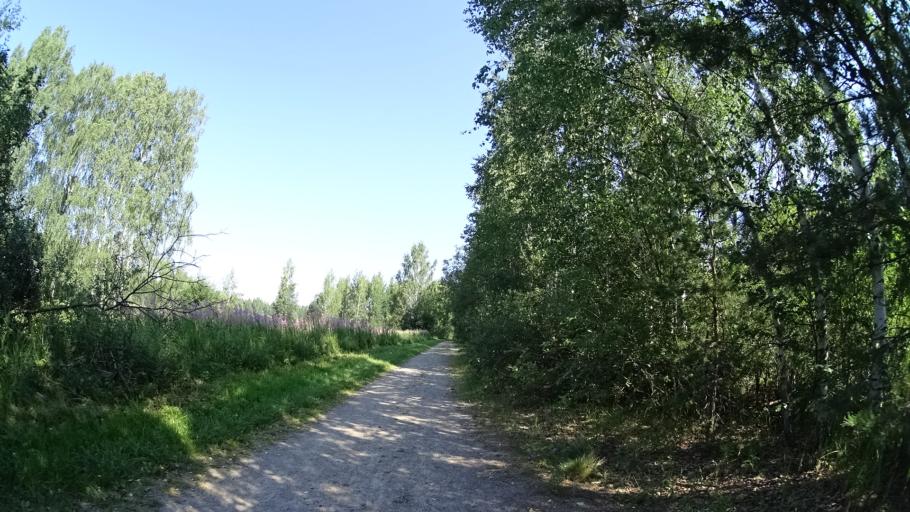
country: FI
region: Uusimaa
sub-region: Helsinki
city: Kerava
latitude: 60.3506
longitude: 25.1263
